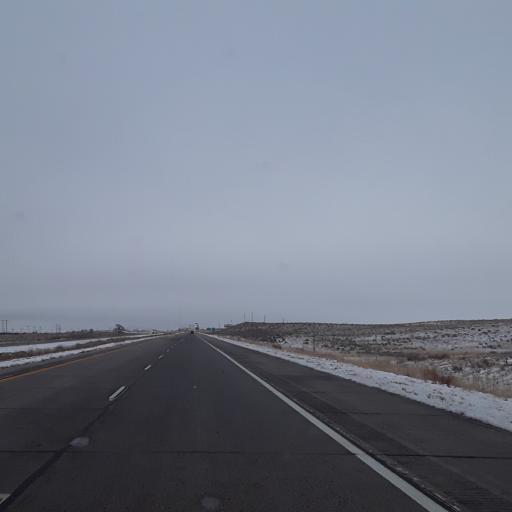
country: US
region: Colorado
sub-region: Logan County
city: Sterling
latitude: 40.6040
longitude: -103.1823
